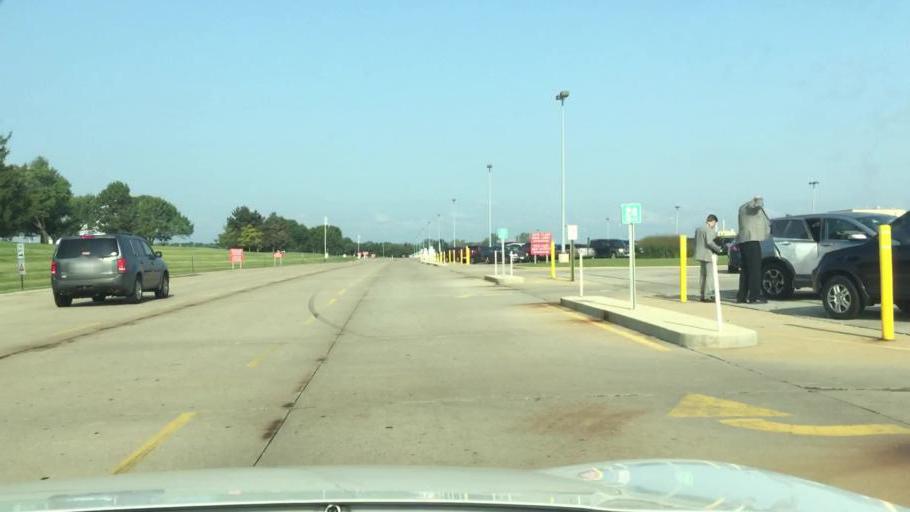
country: US
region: Ohio
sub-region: Champaign County
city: North Lewisburg
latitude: 40.2751
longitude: -83.5072
